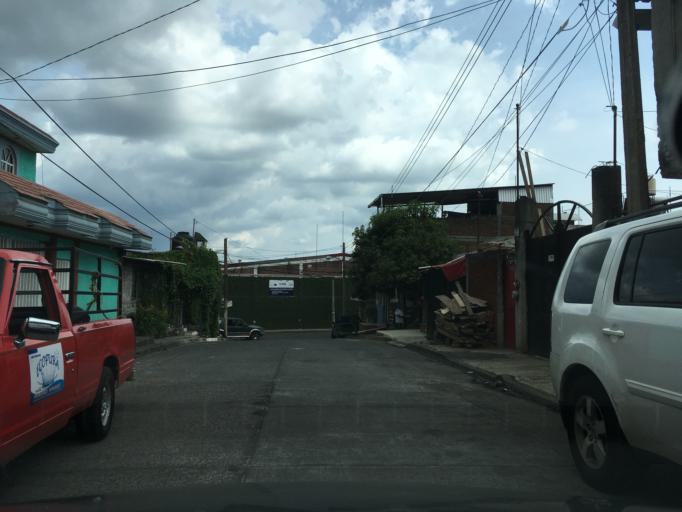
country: MX
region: Michoacan
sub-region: Uruapan
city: Uruapan
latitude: 19.4244
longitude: -102.0427
